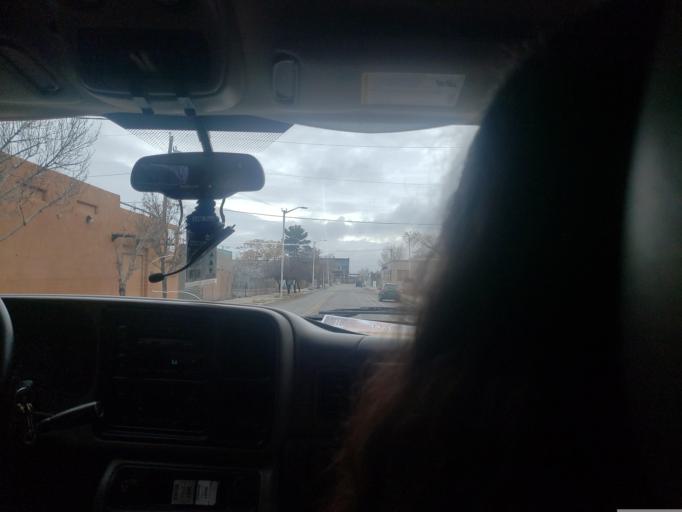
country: US
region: New Mexico
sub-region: Bernalillo County
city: Albuquerque
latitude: 35.0792
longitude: -106.6503
